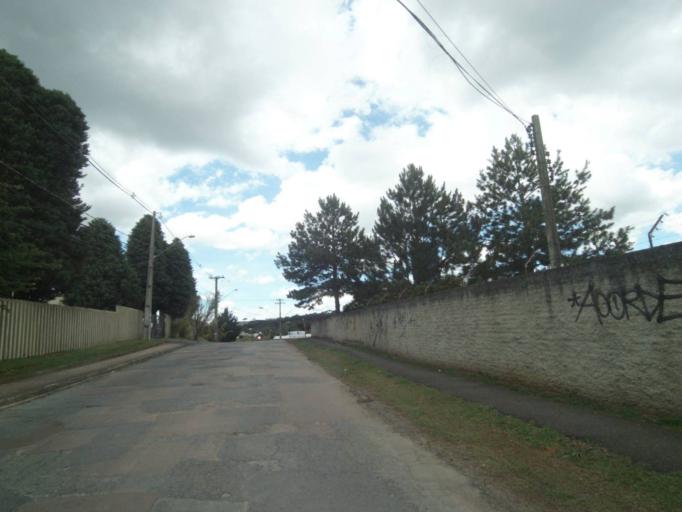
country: BR
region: Parana
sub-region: Curitiba
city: Curitiba
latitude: -25.4315
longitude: -49.3389
